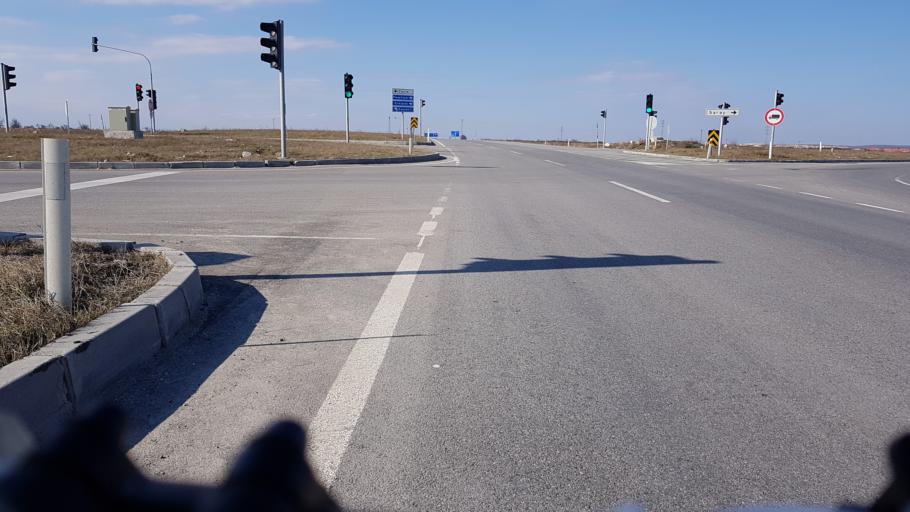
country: TR
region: Tekirdag
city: Saray
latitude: 41.4310
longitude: 27.9097
